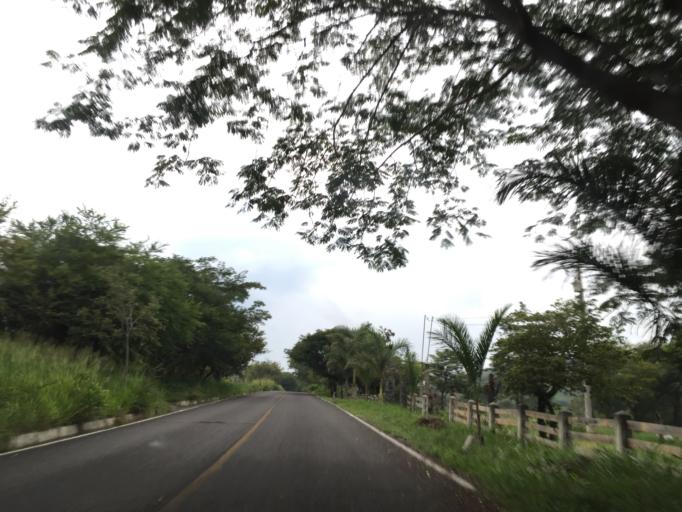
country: MX
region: Colima
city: Comala
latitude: 19.3883
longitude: -103.8010
